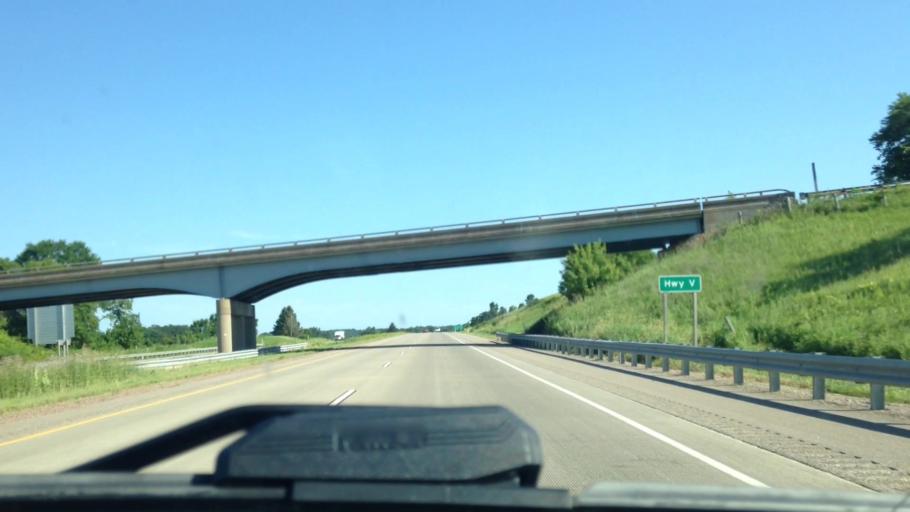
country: US
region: Wisconsin
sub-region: Eau Claire County
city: Fall Creek
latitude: 44.6607
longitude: -91.3147
